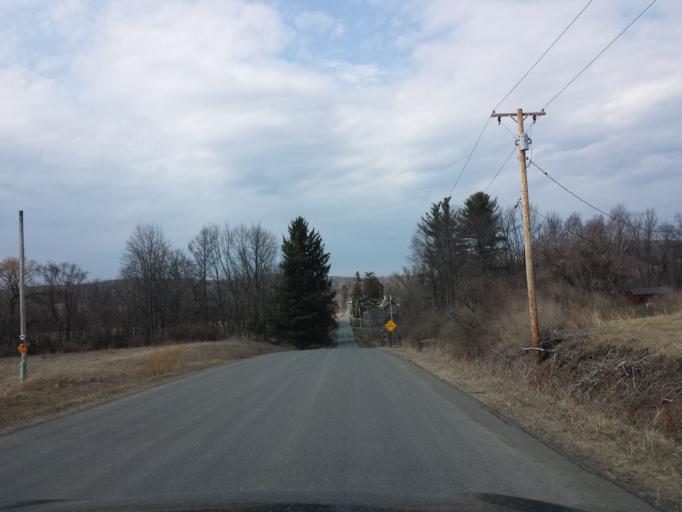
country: US
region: New York
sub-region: Tompkins County
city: Dryden
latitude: 42.3901
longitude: -76.3503
